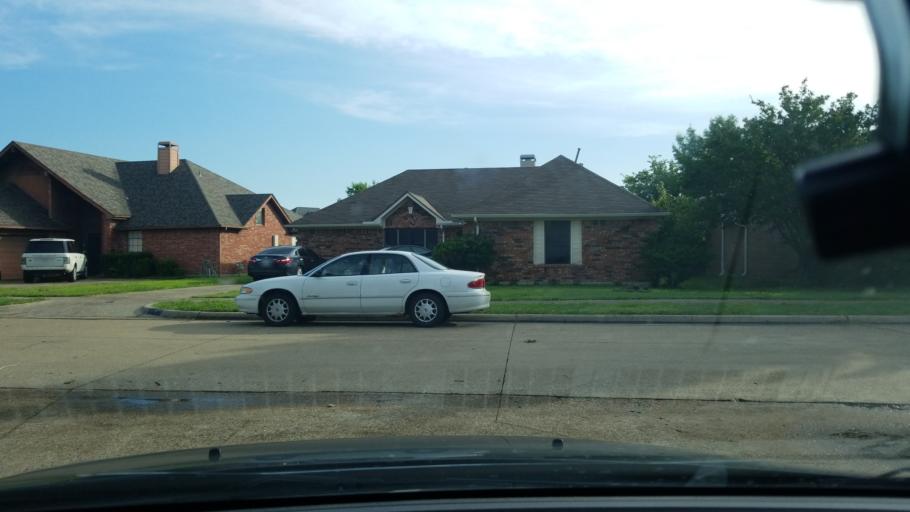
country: US
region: Texas
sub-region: Dallas County
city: Mesquite
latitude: 32.7989
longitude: -96.6045
